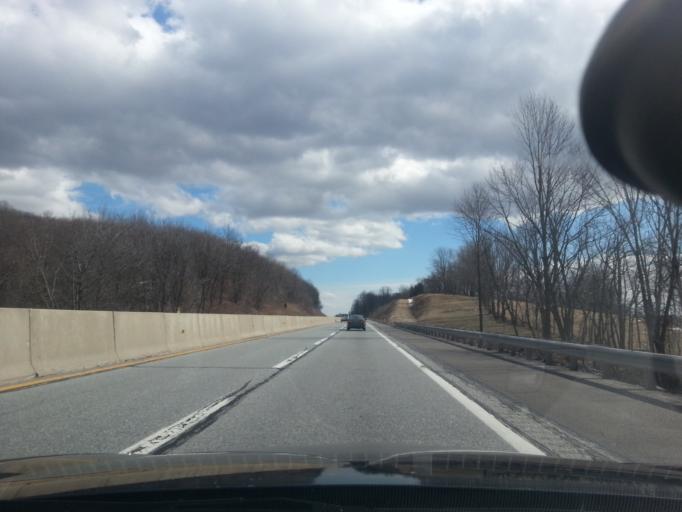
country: US
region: Pennsylvania
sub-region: Bucks County
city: Spinnerstown
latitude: 40.4795
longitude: -75.4603
